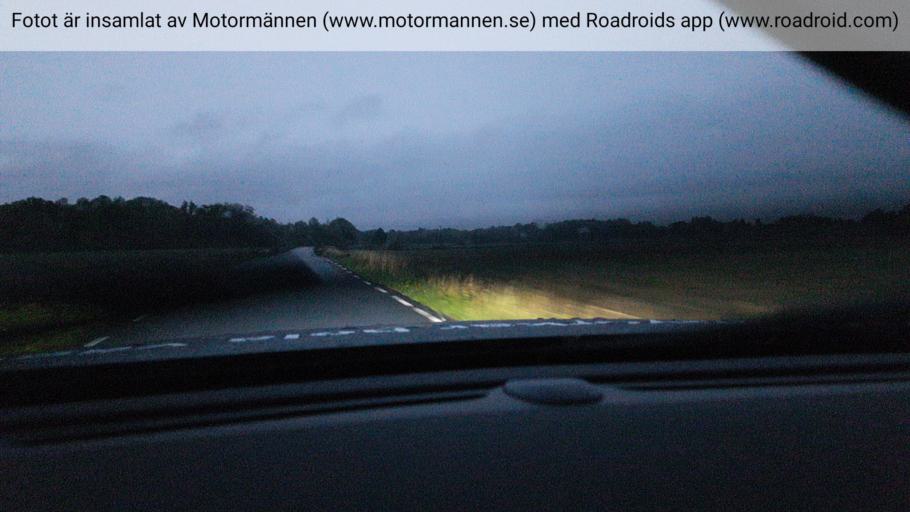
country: SE
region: Vaestra Goetaland
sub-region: Tidaholms Kommun
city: Tidaholm
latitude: 58.1853
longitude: 13.8224
